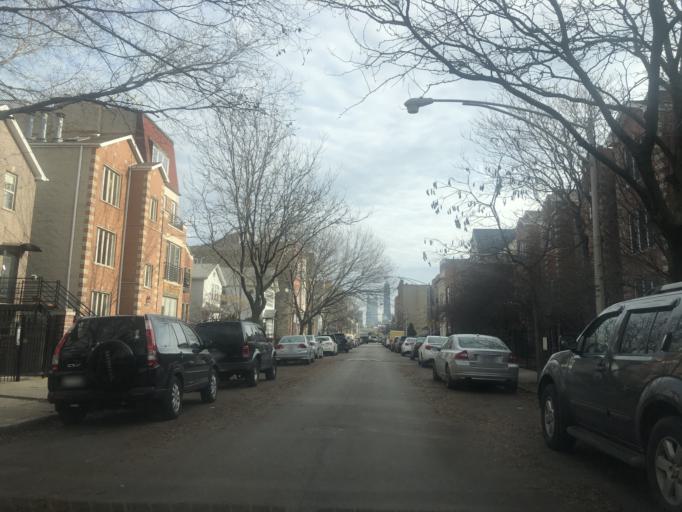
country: US
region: Illinois
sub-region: Cook County
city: Chicago
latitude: 41.8989
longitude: -87.6648
